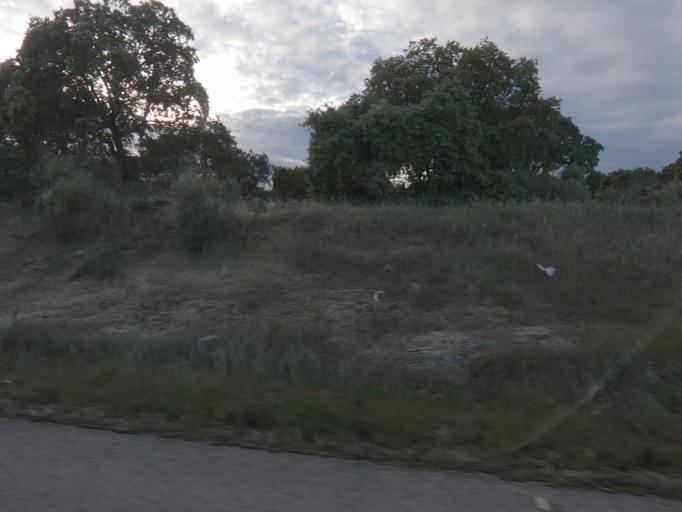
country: ES
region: Extremadura
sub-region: Provincia de Caceres
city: Caceres
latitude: 39.3982
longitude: -6.4228
